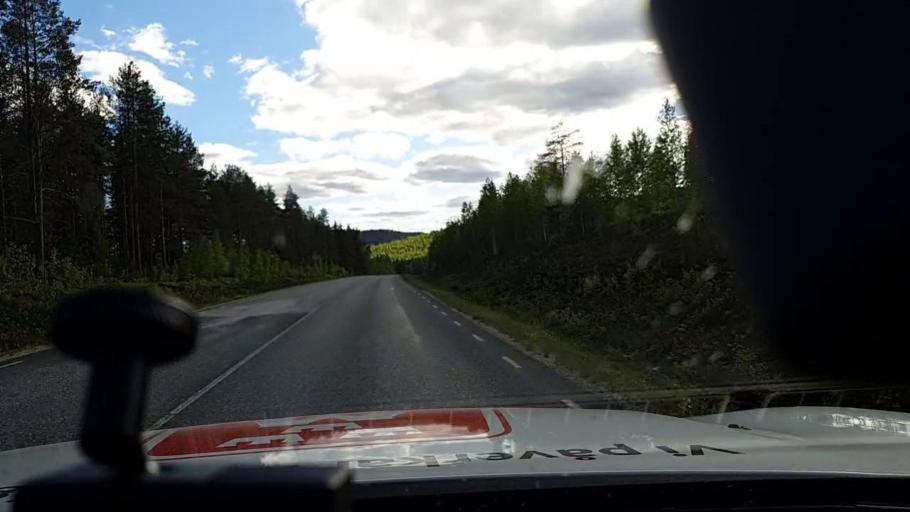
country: FI
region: Lapland
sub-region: Torniolaakso
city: Ylitornio
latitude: 66.3318
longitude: 23.6366
